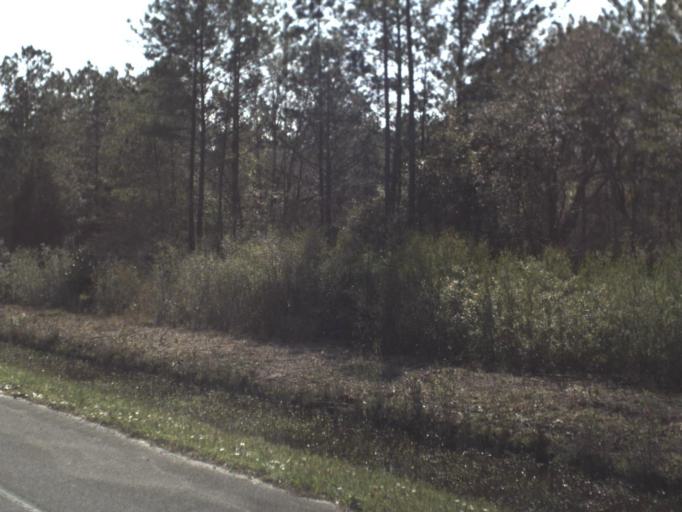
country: US
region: Florida
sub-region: Wakulla County
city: Crawfordville
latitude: 30.0455
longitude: -84.4946
